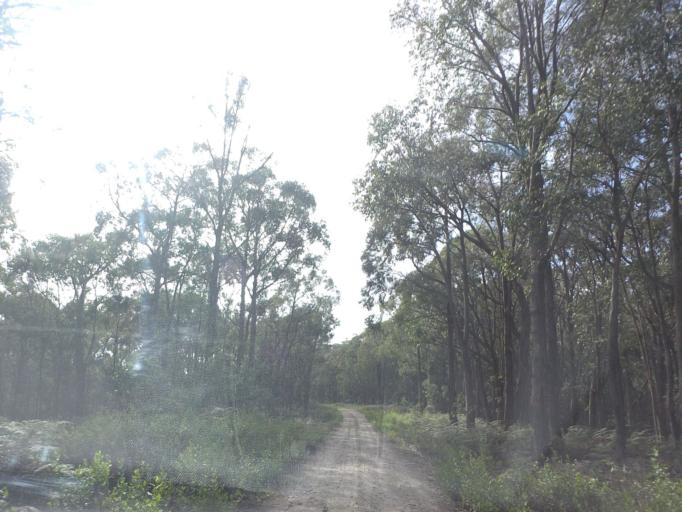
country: AU
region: Victoria
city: Brown Hill
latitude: -37.4915
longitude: 144.1850
